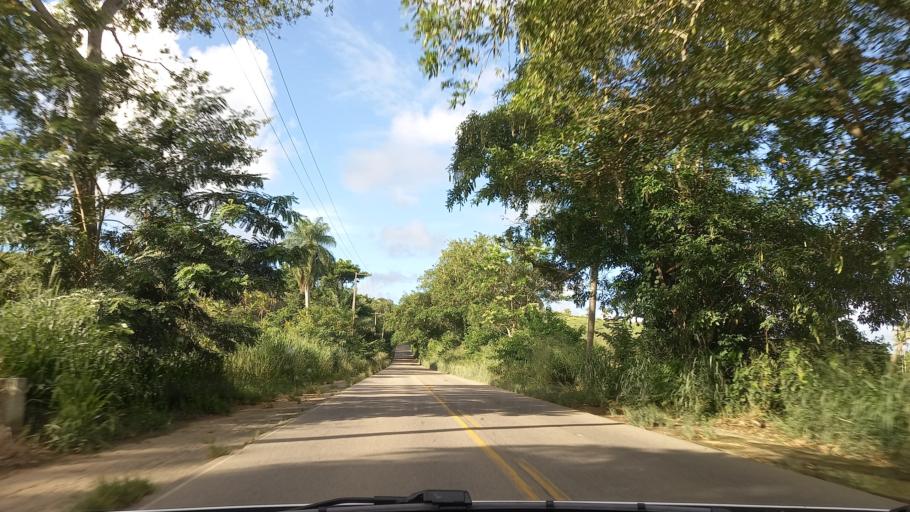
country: BR
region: Pernambuco
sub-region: Rio Formoso
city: Rio Formoso
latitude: -8.6550
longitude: -35.1366
